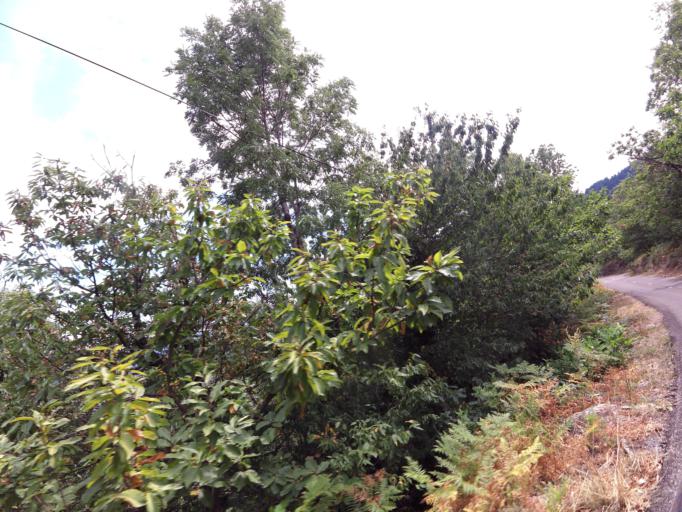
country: FR
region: Languedoc-Roussillon
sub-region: Departement du Gard
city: Valleraugue
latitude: 44.0326
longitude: 3.6211
